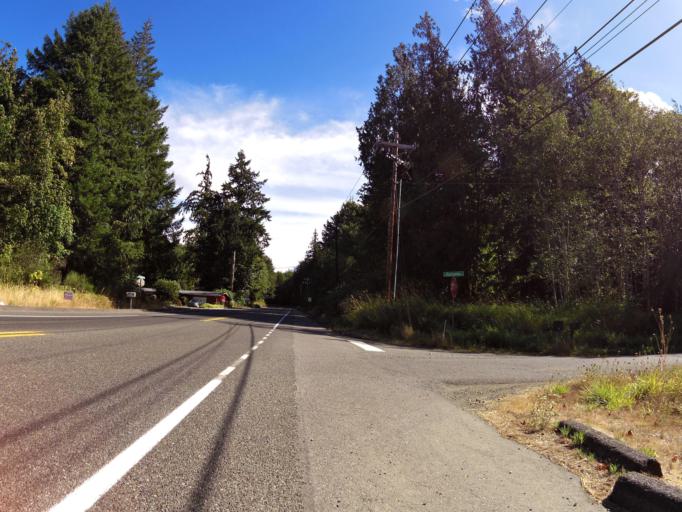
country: US
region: Washington
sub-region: Mason County
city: Shelton
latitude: 47.1259
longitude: -123.0922
